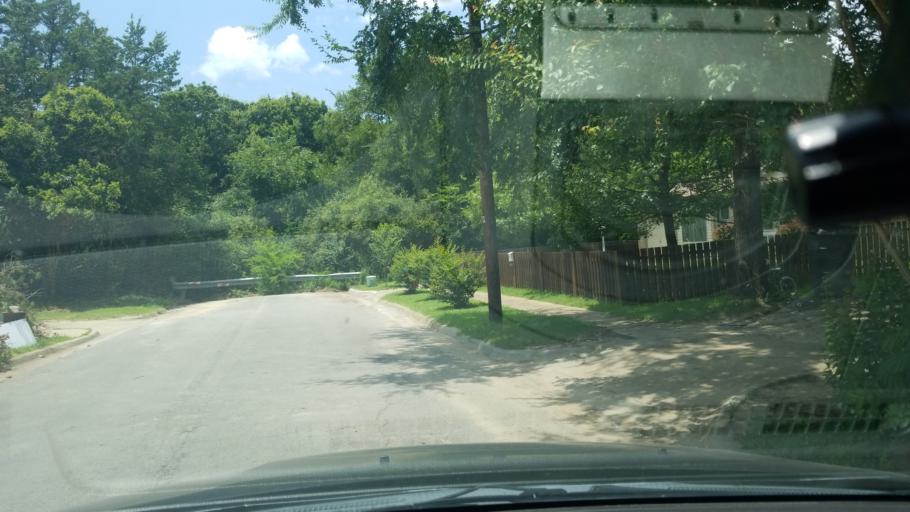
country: US
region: Texas
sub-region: Dallas County
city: Balch Springs
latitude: 32.7149
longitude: -96.6535
